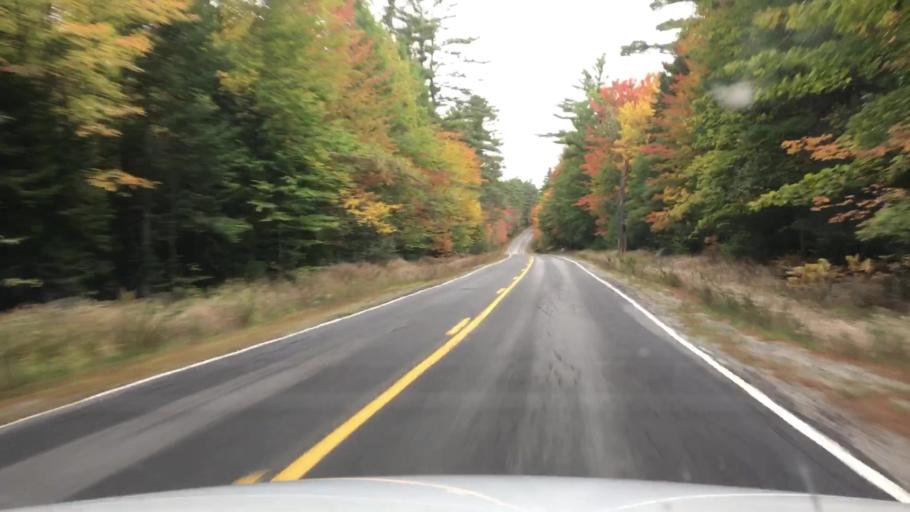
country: US
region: Maine
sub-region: Oxford County
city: Bethel
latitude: 44.3824
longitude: -70.7987
